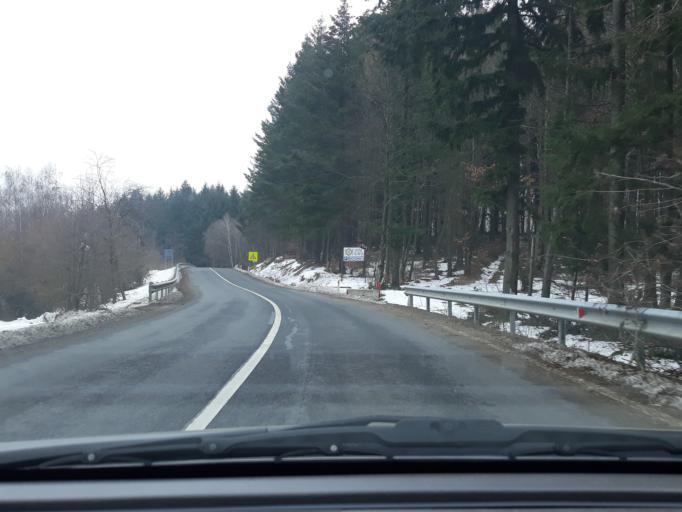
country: RO
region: Bihor
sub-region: Comuna Sinteu
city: Sinteu
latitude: 47.1206
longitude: 22.4412
